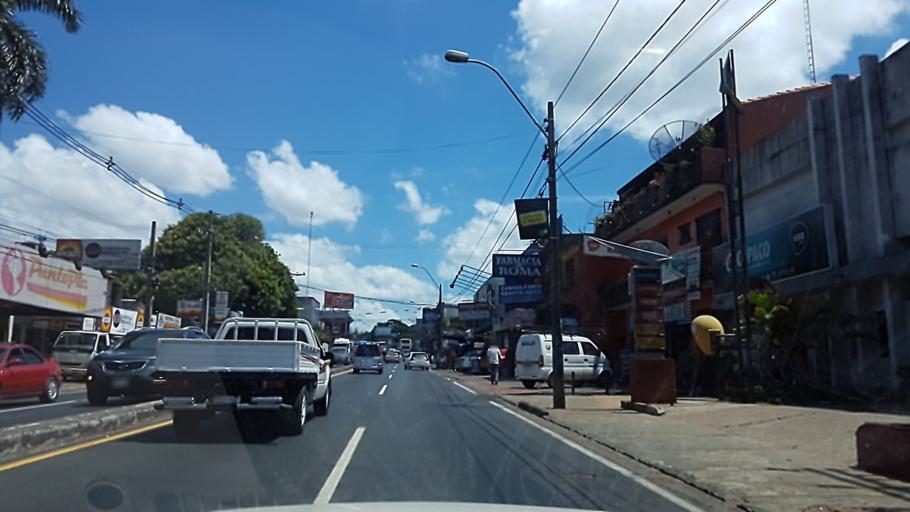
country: PY
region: Central
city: Capiata
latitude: -25.3544
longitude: -57.4422
